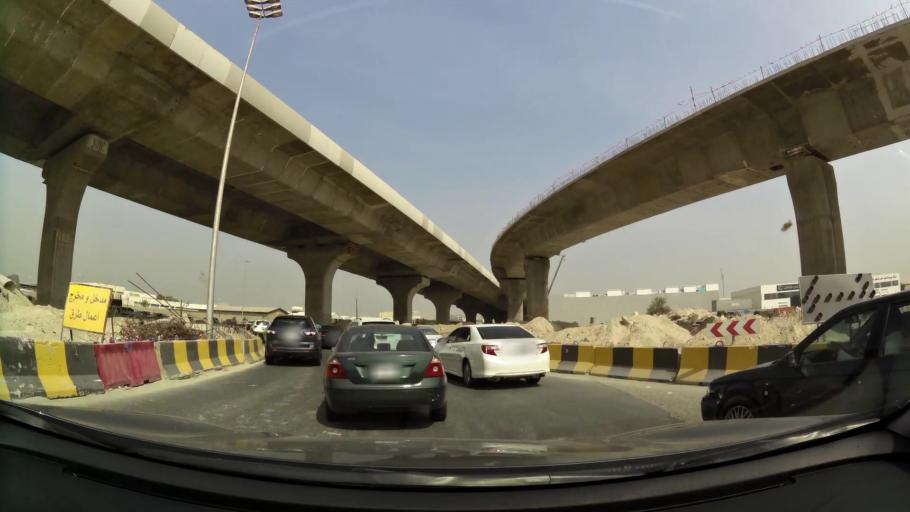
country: KW
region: Al Asimah
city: Ash Shamiyah
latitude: 29.3319
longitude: 47.9315
